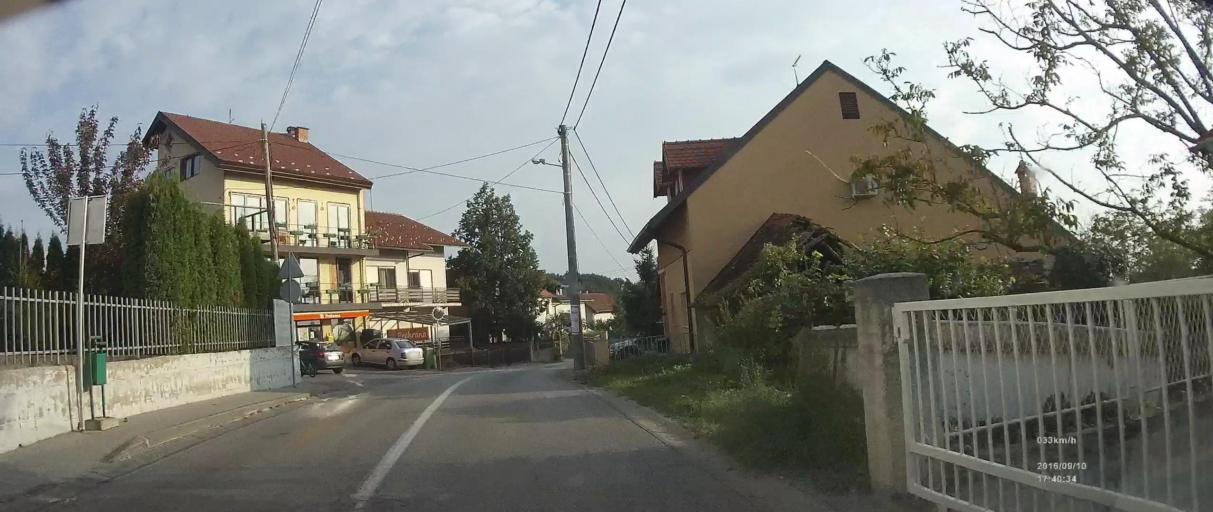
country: HR
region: Grad Zagreb
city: Zagreb
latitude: 45.8387
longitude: 15.9357
